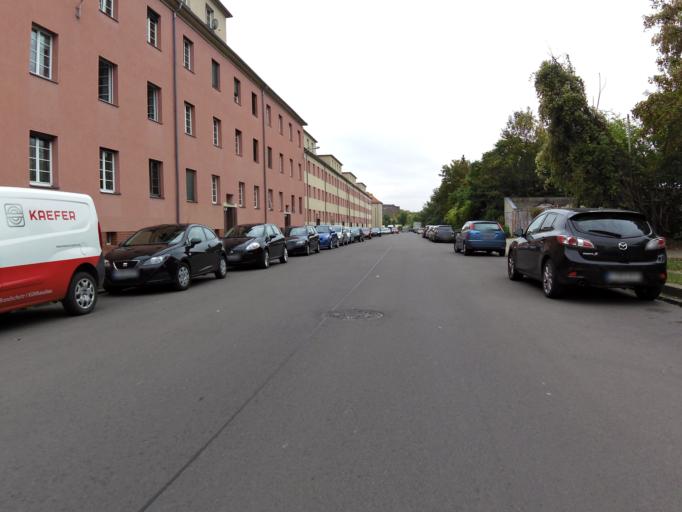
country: DE
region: Saxony
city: Leipzig
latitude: 51.3295
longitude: 12.3133
